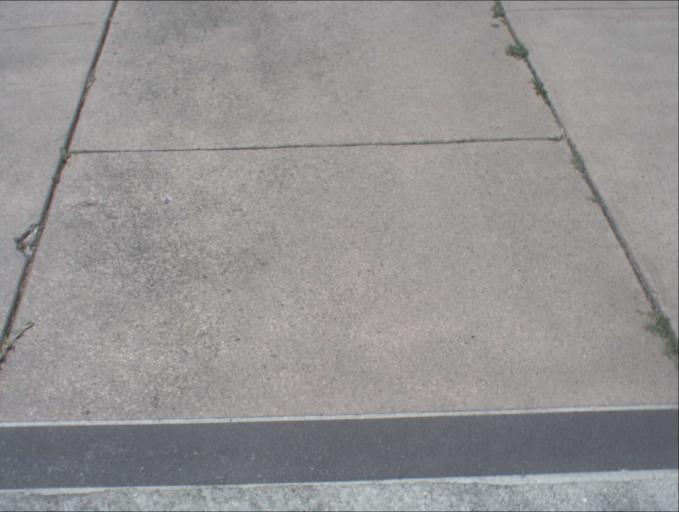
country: AU
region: Queensland
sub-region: Logan
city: Windaroo
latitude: -27.7493
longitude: 153.1841
